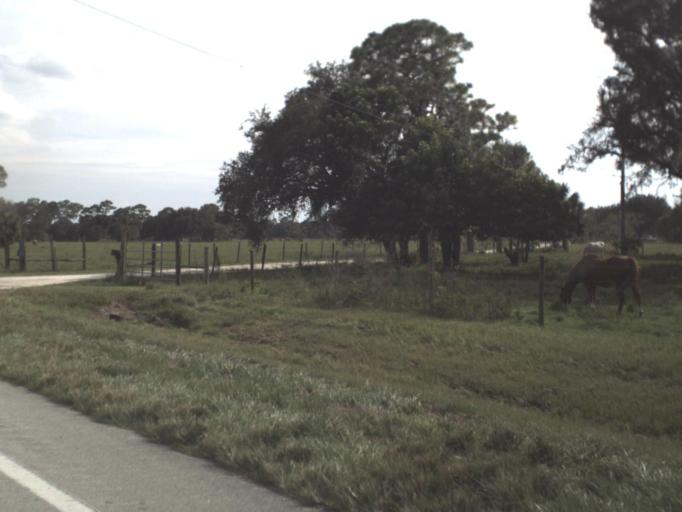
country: US
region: Florida
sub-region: Okeechobee County
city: Taylor Creek
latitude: 27.2324
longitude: -80.7754
